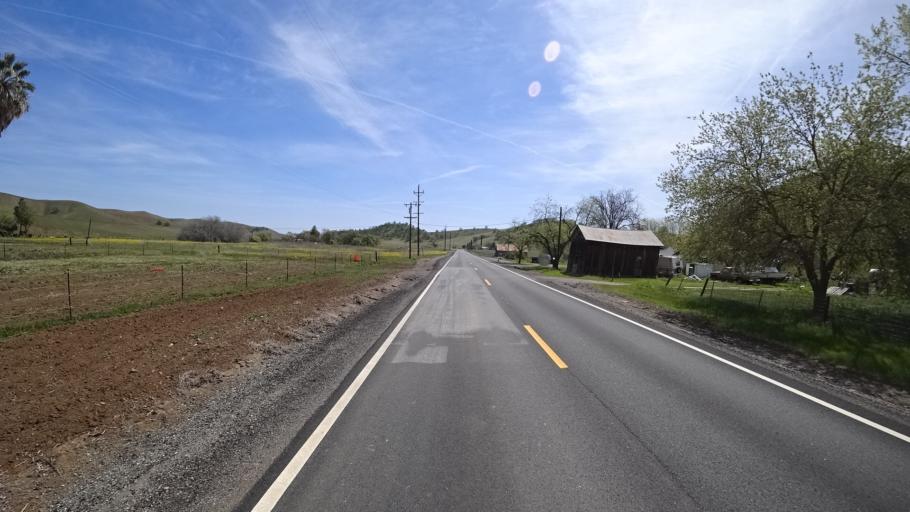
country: US
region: California
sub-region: Glenn County
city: Willows
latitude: 39.5891
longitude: -122.4516
